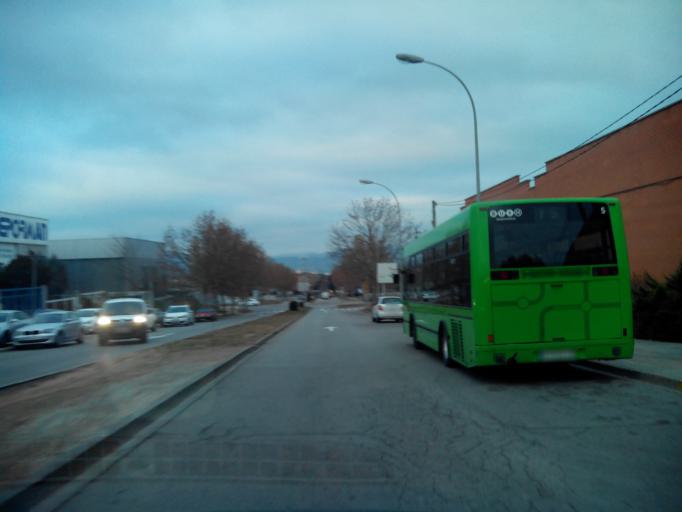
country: ES
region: Catalonia
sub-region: Provincia de Barcelona
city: Manresa
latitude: 41.7167
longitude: 1.8482
